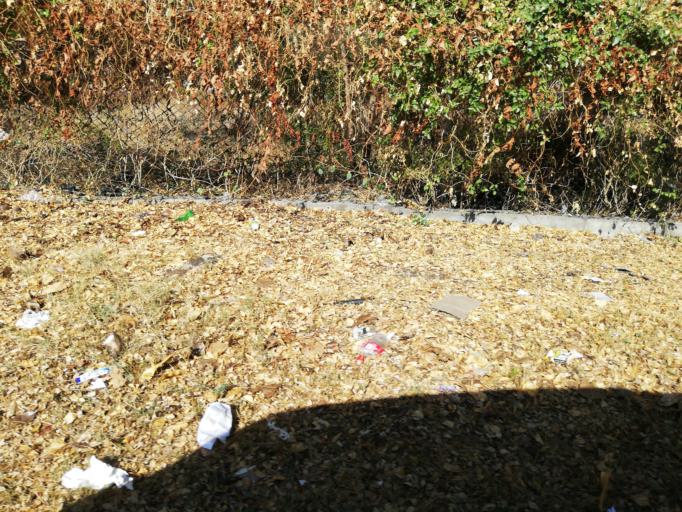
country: MU
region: Port Louis
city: Port Louis
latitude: -20.1622
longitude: 57.4928
